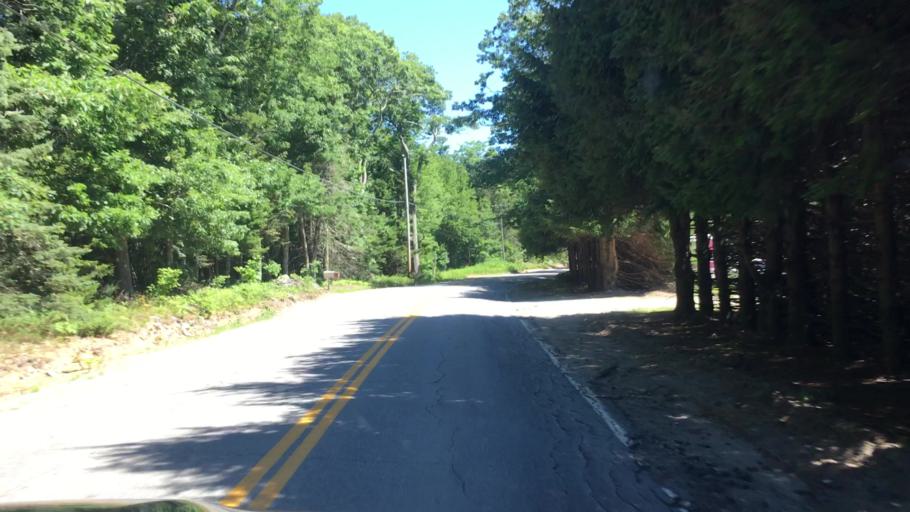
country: US
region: Maine
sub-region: Hancock County
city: Penobscot
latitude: 44.4370
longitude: -68.7119
